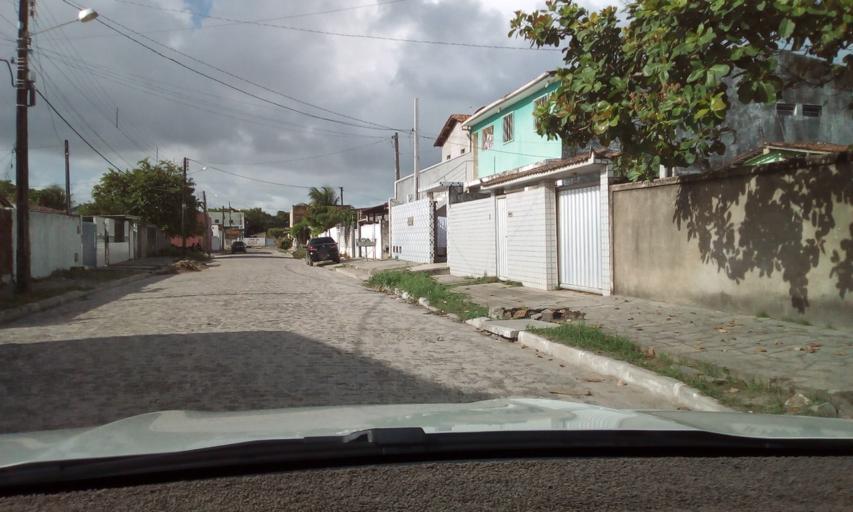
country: BR
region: Paraiba
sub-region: Joao Pessoa
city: Joao Pessoa
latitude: -7.1783
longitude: -34.8313
